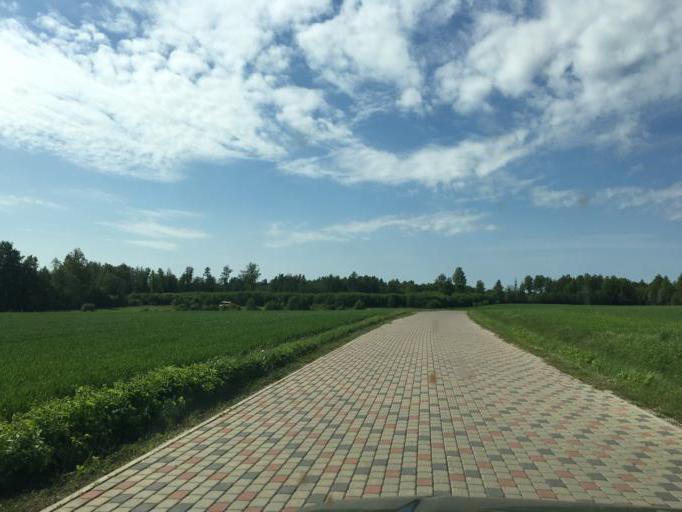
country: LV
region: Talsu Rajons
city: Valdemarpils
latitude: 57.3755
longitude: 22.5201
